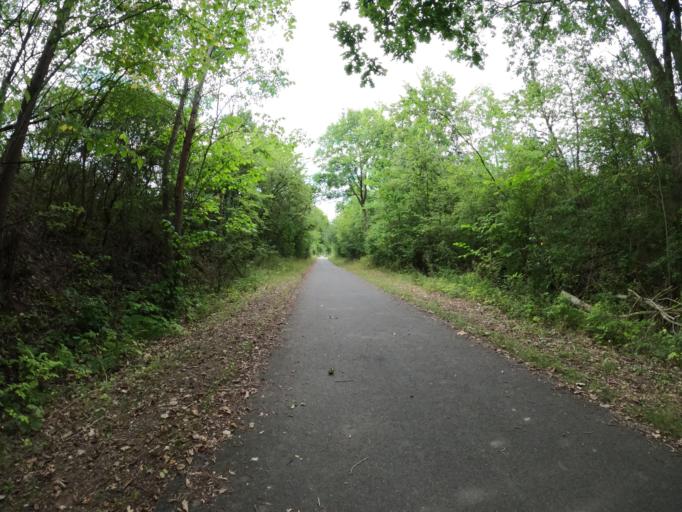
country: DE
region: Mecklenburg-Vorpommern
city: Woldegk
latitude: 53.3681
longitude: 13.5893
